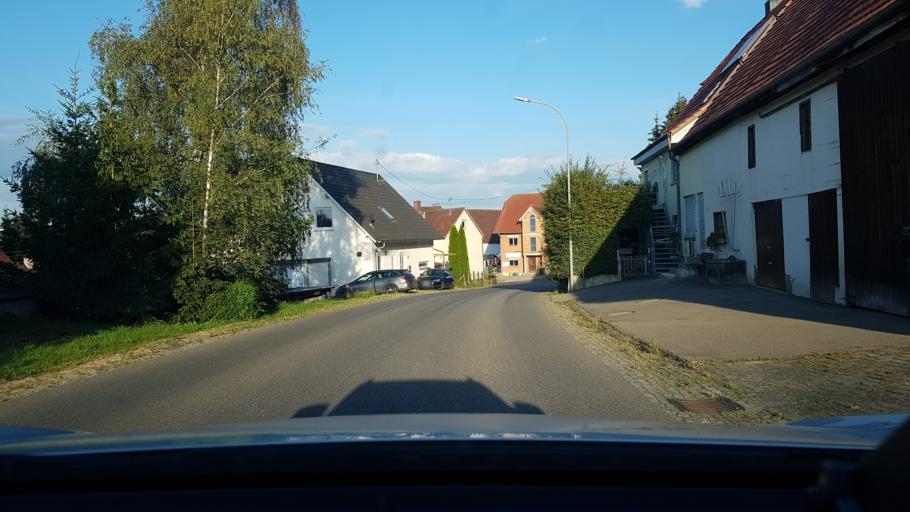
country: DE
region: Baden-Wuerttemberg
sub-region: Tuebingen Region
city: Warthausen
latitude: 48.1745
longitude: 9.8039
